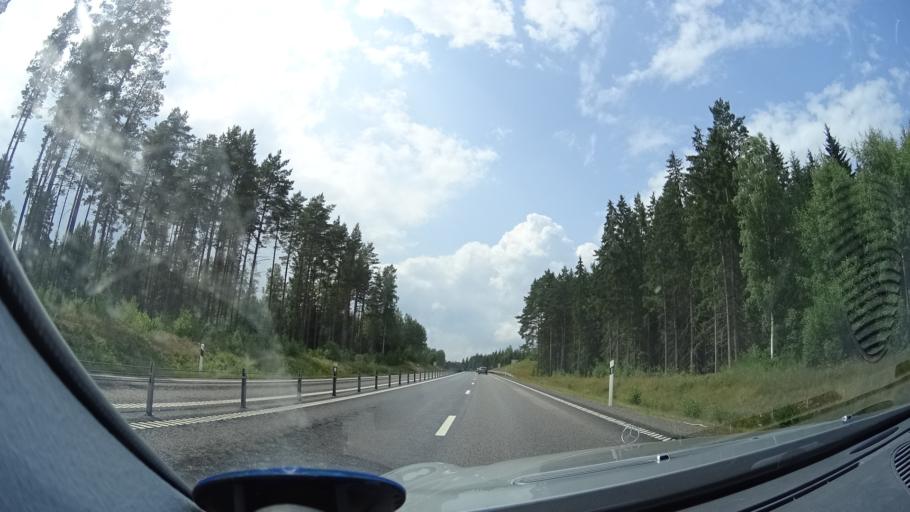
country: SE
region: Kalmar
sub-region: Nybro Kommun
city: Nybro
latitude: 56.7245
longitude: 15.8124
